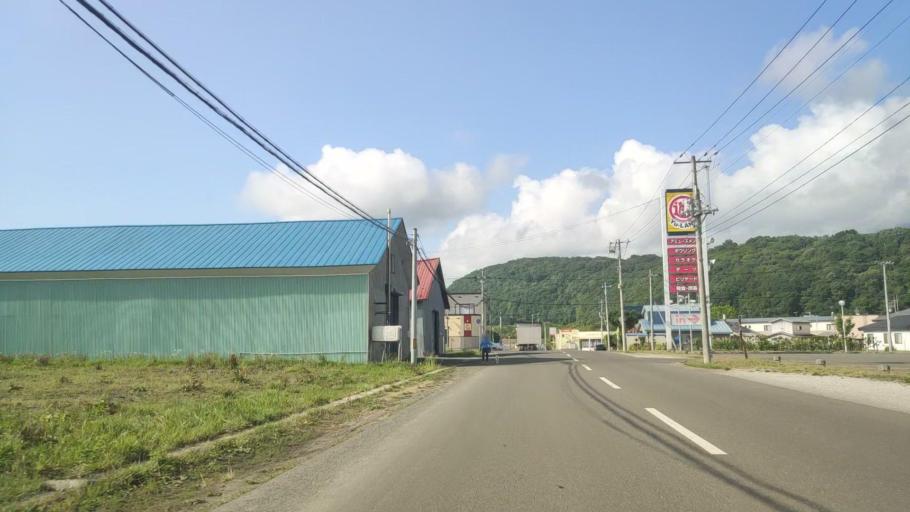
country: JP
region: Hokkaido
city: Shimo-furano
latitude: 43.3436
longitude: 142.3806
